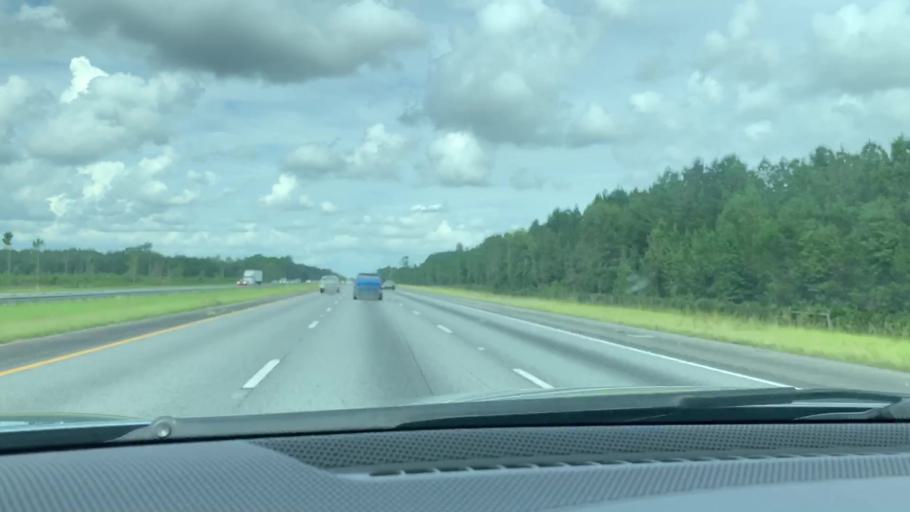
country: US
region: Georgia
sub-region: Liberty County
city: Midway
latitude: 31.6133
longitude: -81.4149
